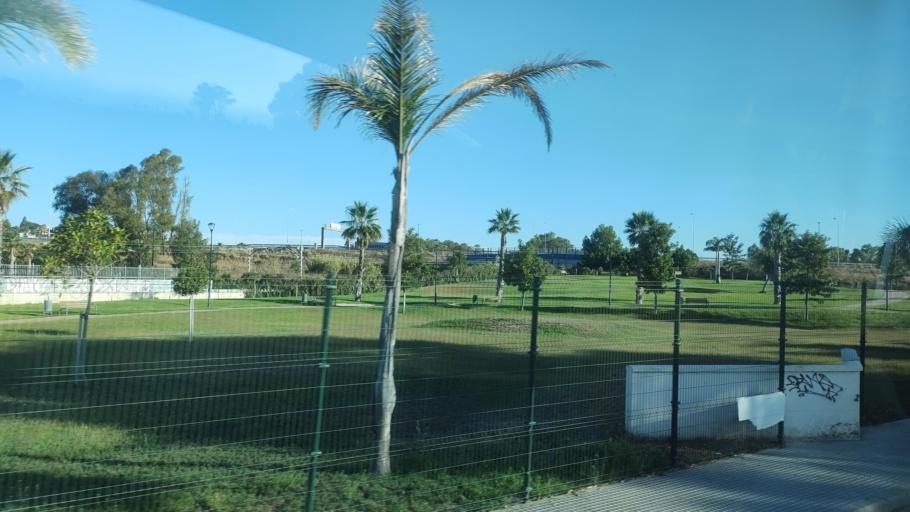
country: ES
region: Andalusia
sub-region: Provincia de Malaga
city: Torremolinos
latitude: 36.6473
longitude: -4.4835
